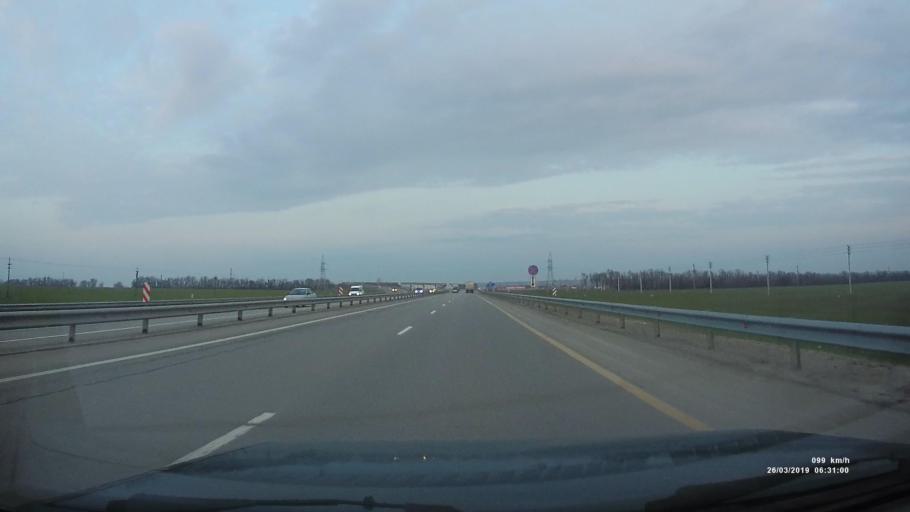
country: RU
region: Rostov
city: Krym
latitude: 47.2726
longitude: 39.5409
